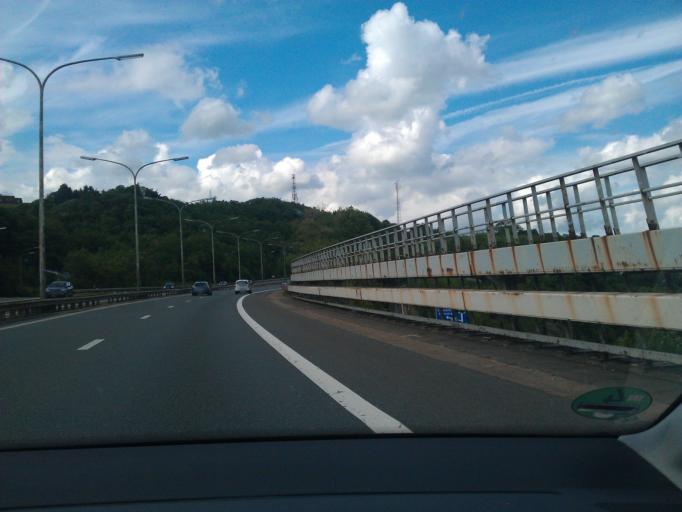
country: BE
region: Wallonia
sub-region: Province de Liege
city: Verviers
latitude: 50.5931
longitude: 5.8439
